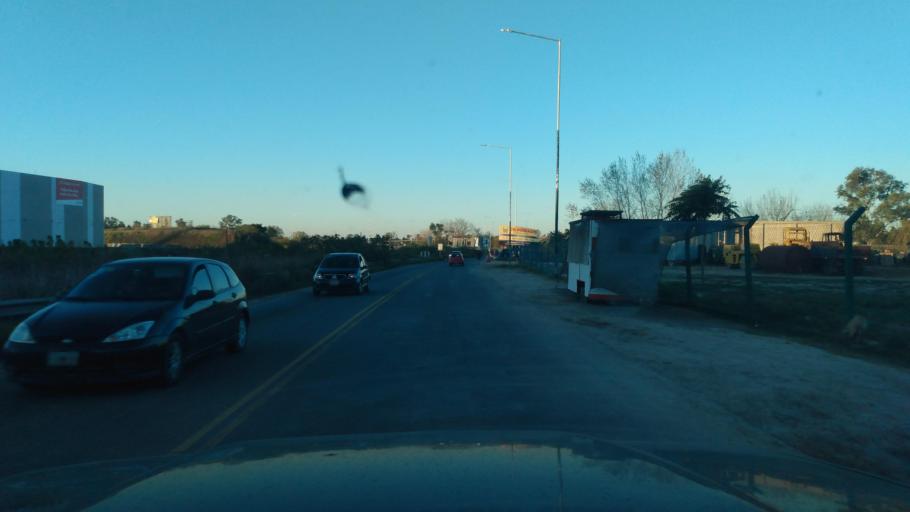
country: AR
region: Buenos Aires
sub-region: Partido de Merlo
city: Merlo
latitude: -34.6313
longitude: -58.7264
